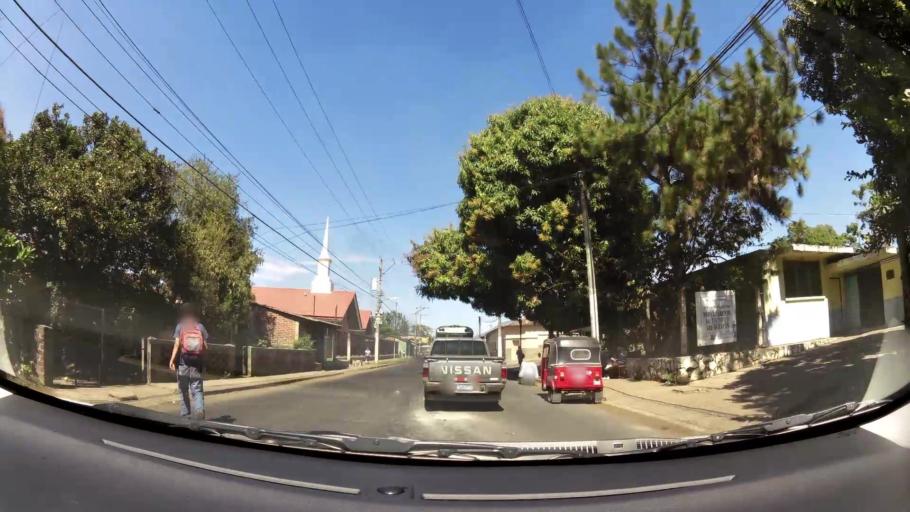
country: SV
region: Ahuachapan
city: Atiquizaya
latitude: 13.9717
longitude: -89.7548
